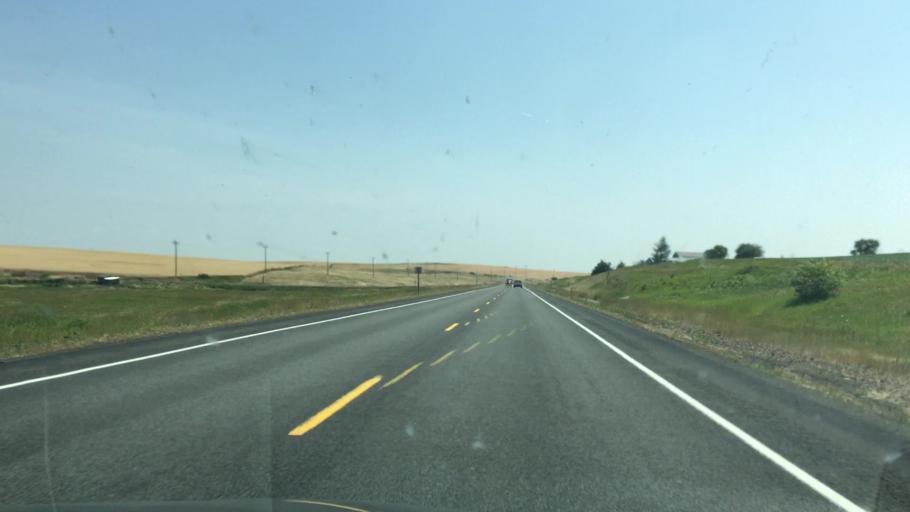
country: US
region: Idaho
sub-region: Lewis County
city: Nezperce
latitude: 46.2302
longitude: -116.4567
